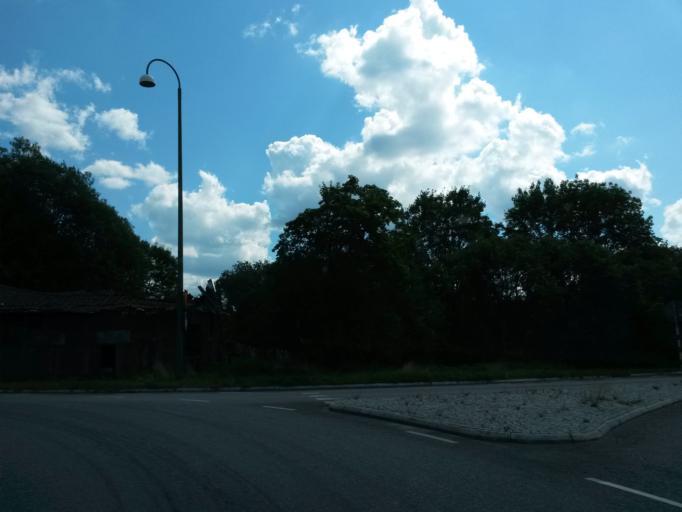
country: SE
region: Vaestra Goetaland
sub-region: Lerums Kommun
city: Stenkullen
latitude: 57.7950
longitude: 12.3179
